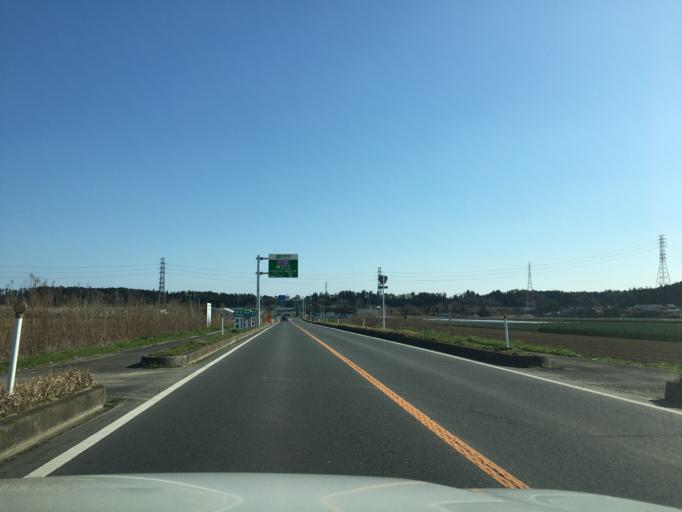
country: JP
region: Ibaraki
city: Mito-shi
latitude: 36.4216
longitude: 140.4230
